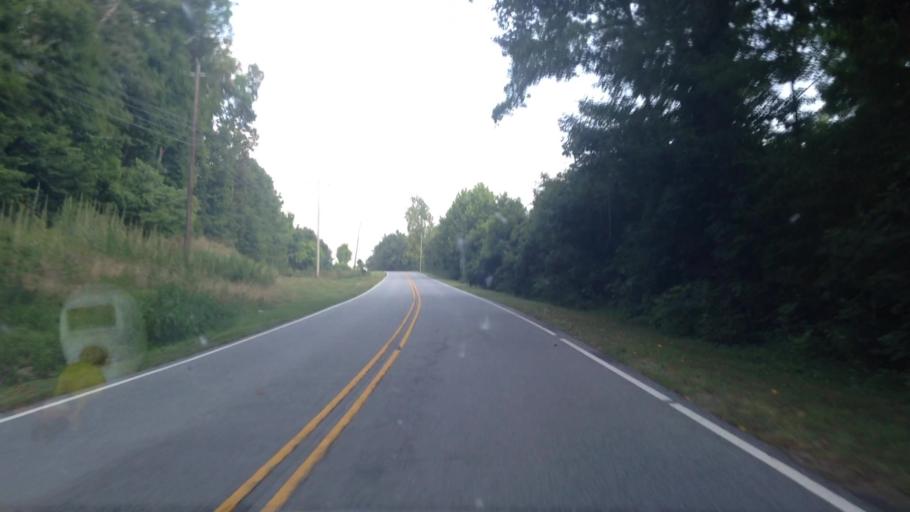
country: US
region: North Carolina
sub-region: Guilford County
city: High Point
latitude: 35.9641
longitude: -80.0784
